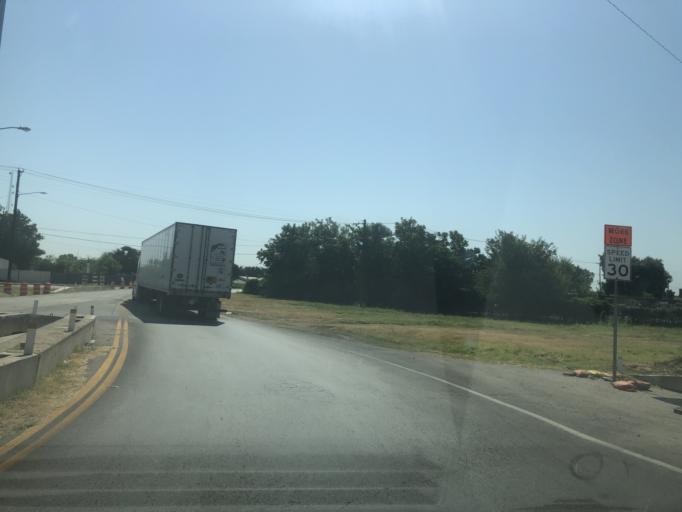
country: US
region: Texas
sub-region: Tarrant County
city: River Oaks
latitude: 32.7748
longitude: -97.3447
